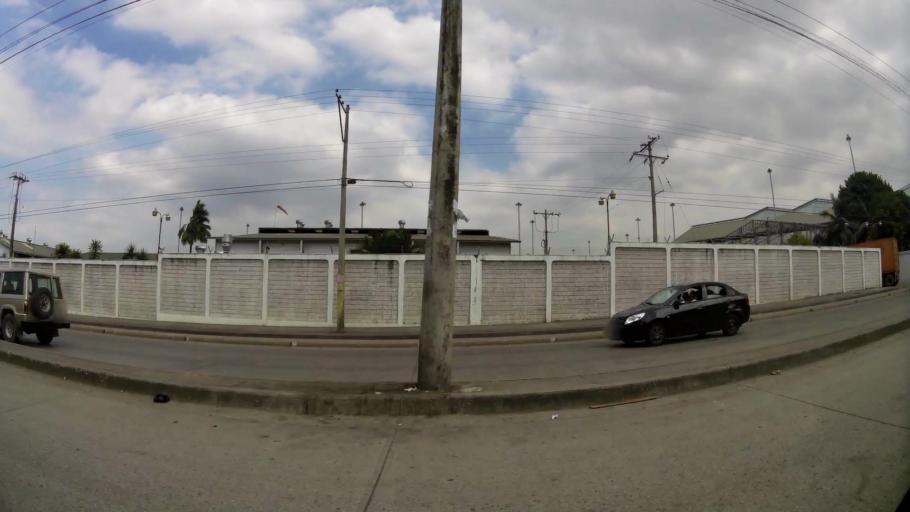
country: EC
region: Guayas
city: Santa Lucia
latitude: -2.0918
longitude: -79.9390
